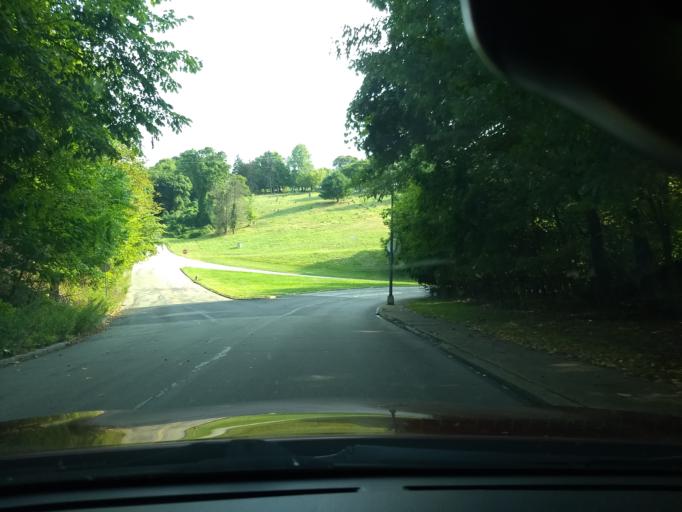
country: US
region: Pennsylvania
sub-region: Allegheny County
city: Aspinwall
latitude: 40.4768
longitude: -79.8986
